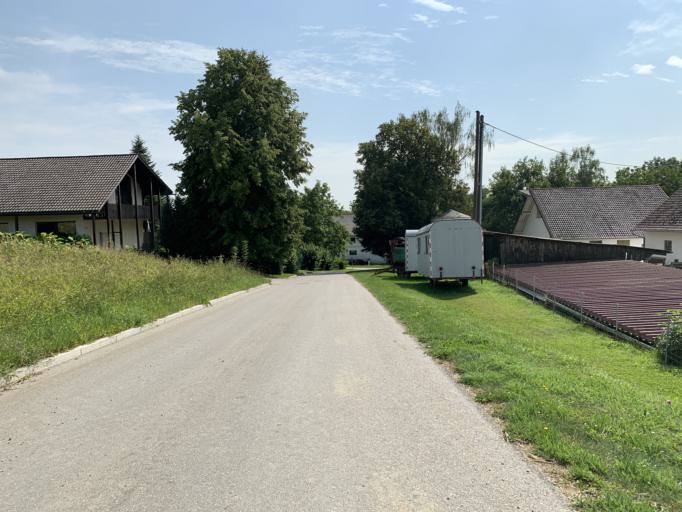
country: DE
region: Bavaria
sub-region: Upper Bavaria
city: Marzling
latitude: 48.4091
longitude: 11.8203
